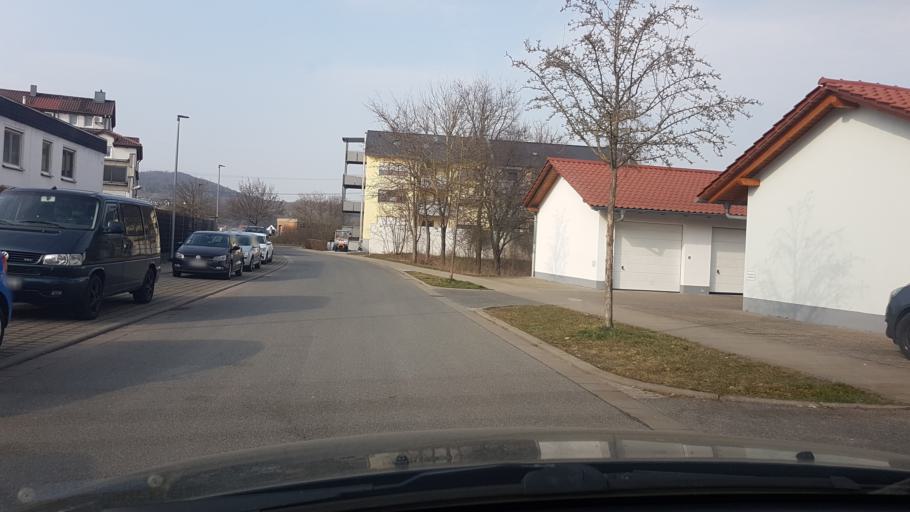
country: DE
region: Bavaria
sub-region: Upper Franconia
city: Hallstadt
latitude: 49.9257
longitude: 10.8669
